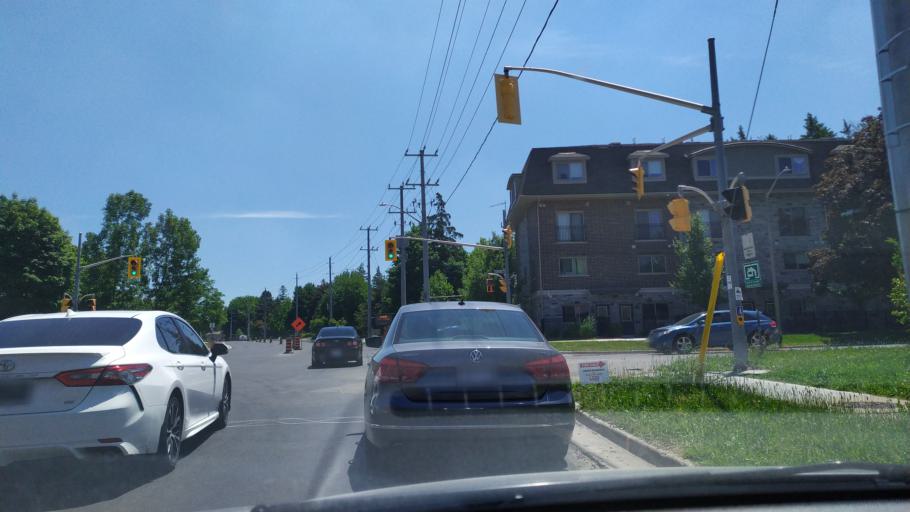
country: CA
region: Ontario
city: Kitchener
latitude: 43.3954
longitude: -80.4460
